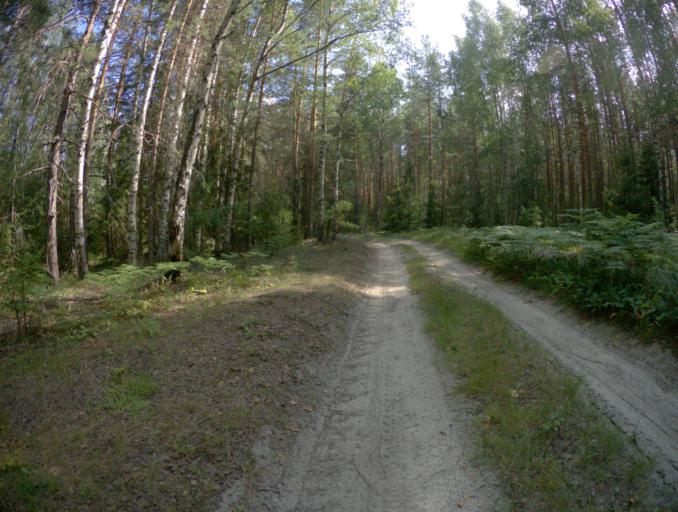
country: RU
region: Vladimir
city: Vorsha
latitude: 55.9118
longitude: 40.1579
